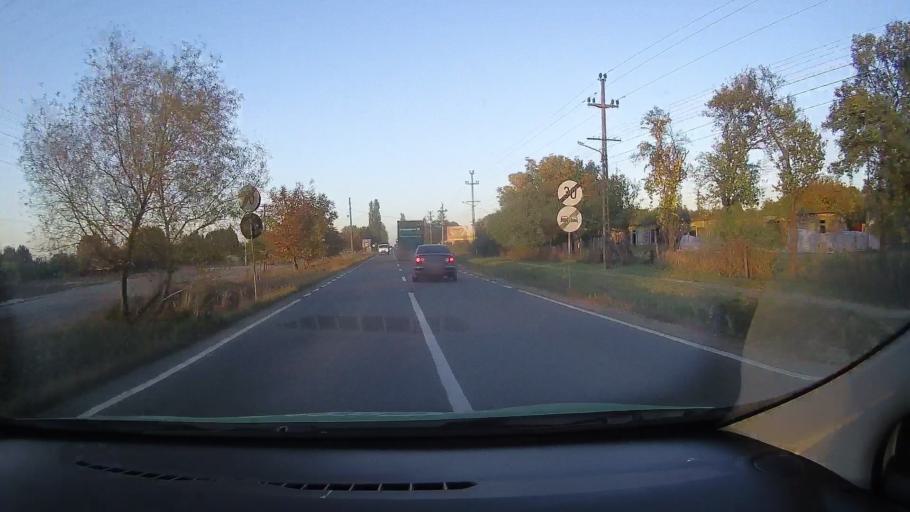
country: RO
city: Dioszeg
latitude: 47.2946
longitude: 22.0117
